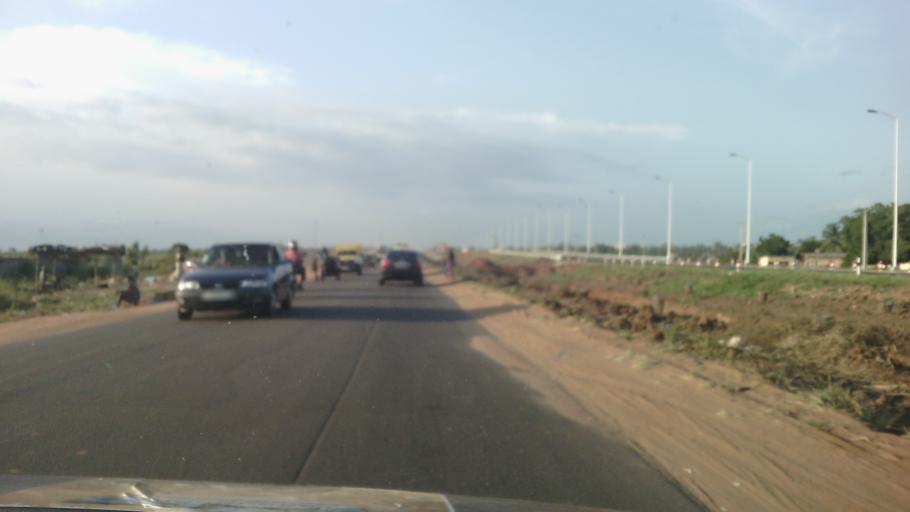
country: TG
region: Maritime
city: Tsevie
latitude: 6.3023
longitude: 1.2145
